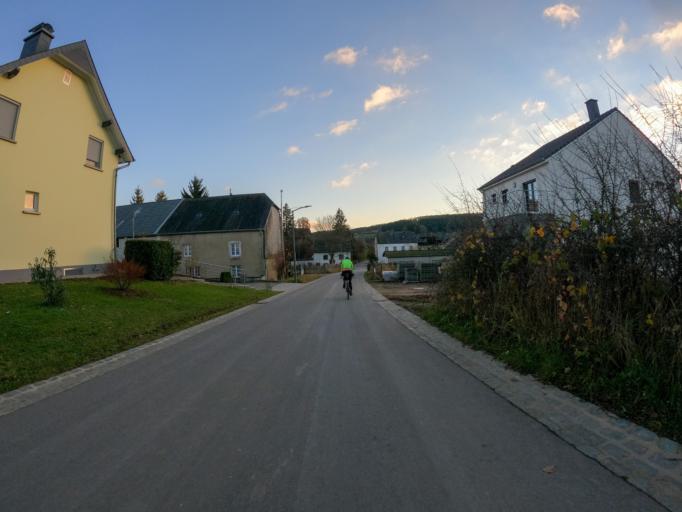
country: LU
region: Diekirch
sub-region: Canton de Wiltz
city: Bavigne
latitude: 49.9249
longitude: 5.8466
